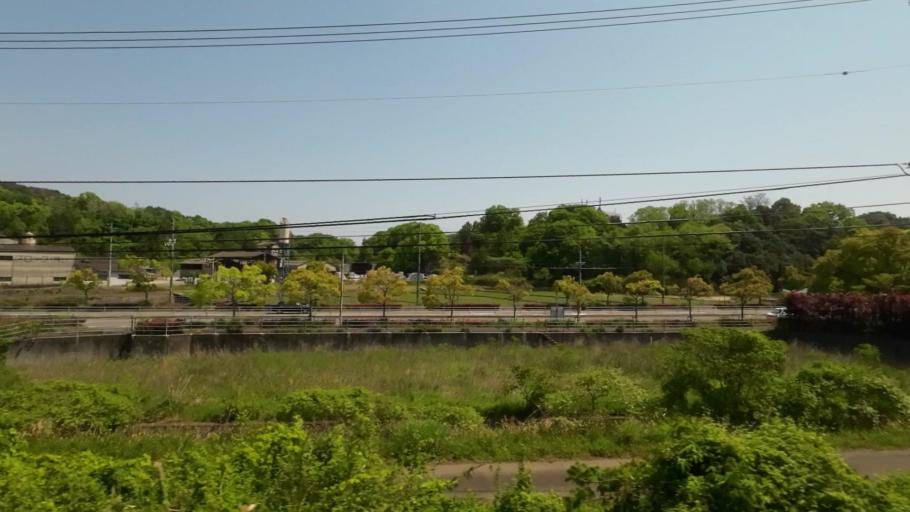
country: JP
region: Ehime
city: Saijo
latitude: 33.9934
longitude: 133.0477
